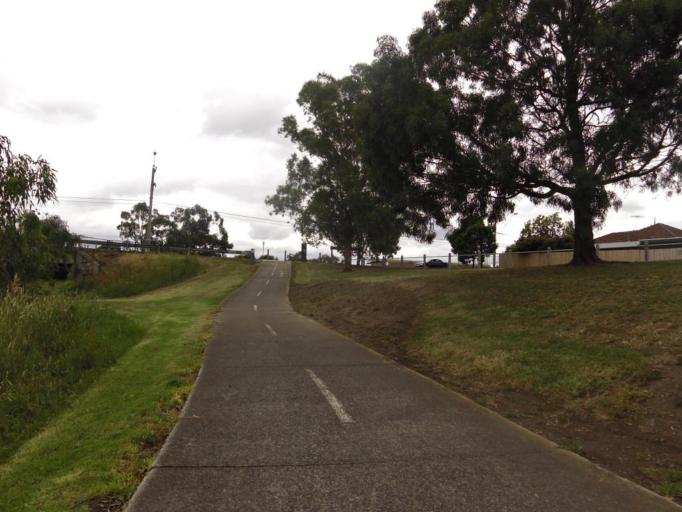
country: AU
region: Victoria
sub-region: Darebin
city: Kingsbury
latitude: -37.7143
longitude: 145.0260
